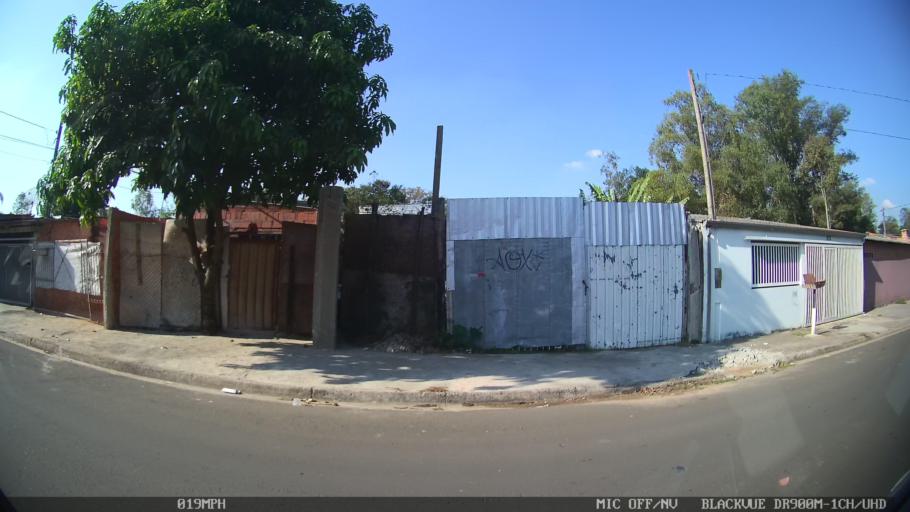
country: BR
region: Sao Paulo
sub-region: Campinas
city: Campinas
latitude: -22.9942
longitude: -47.1381
